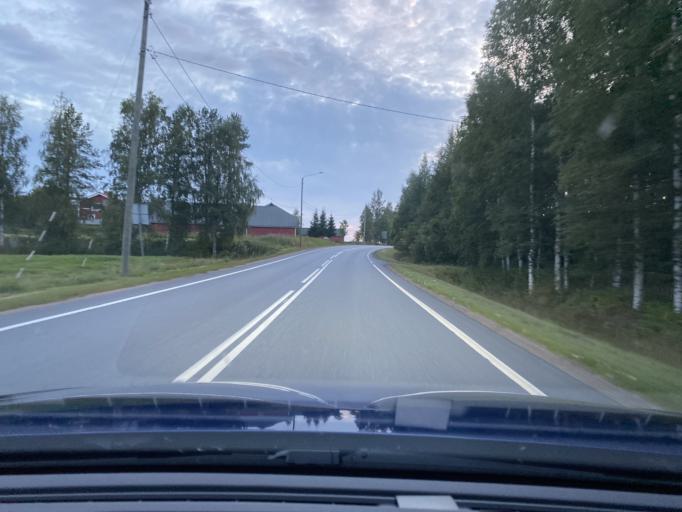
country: FI
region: Satakunta
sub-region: Pohjois-Satakunta
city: Honkajoki
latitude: 62.2140
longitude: 22.2941
